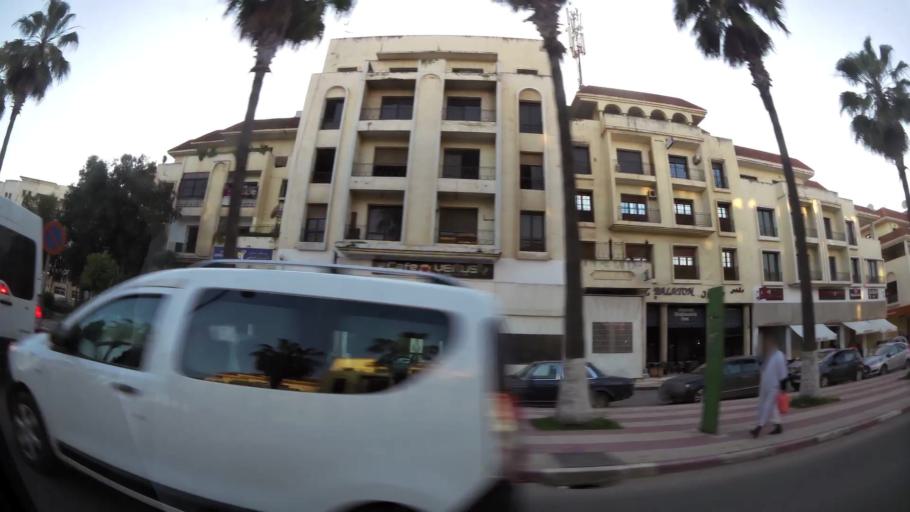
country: MA
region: Chaouia-Ouardigha
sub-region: Settat Province
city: Settat
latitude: 32.9959
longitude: -7.6206
